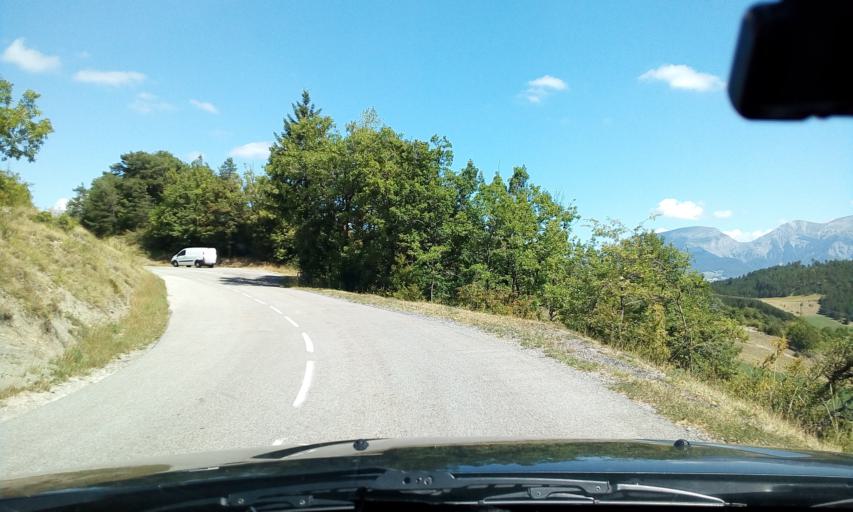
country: FR
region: Rhone-Alpes
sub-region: Departement de l'Isere
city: Mens
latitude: 44.7612
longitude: 5.6702
